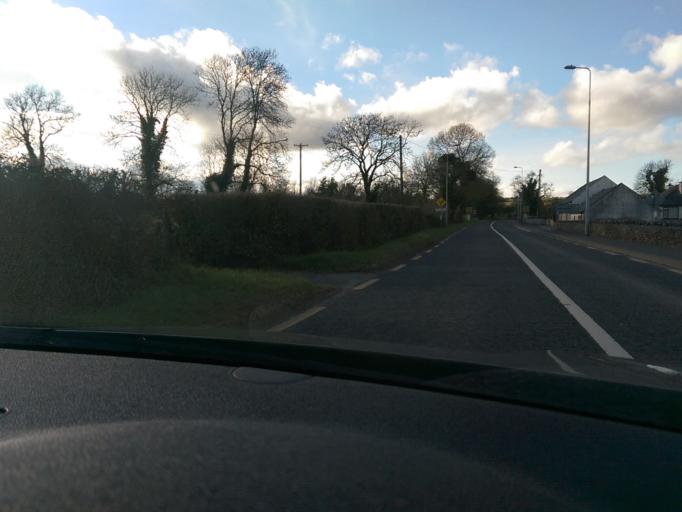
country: IE
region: Connaught
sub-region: Roscommon
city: Roscommon
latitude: 53.6428
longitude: -8.1958
